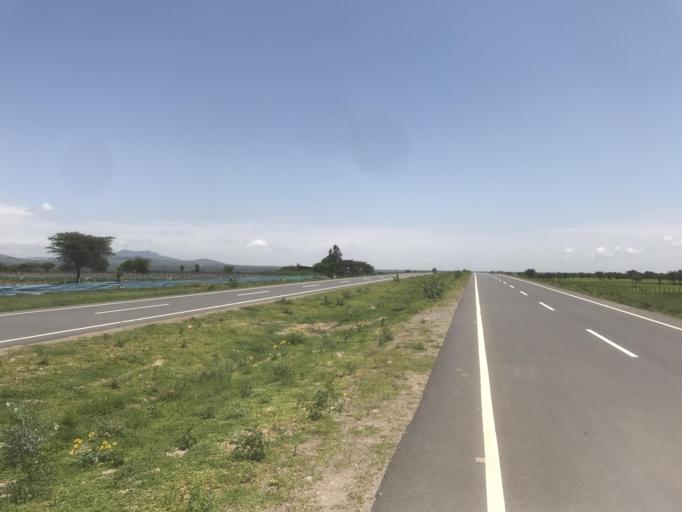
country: ET
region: Oromiya
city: Mojo
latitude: 8.3635
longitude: 38.9919
